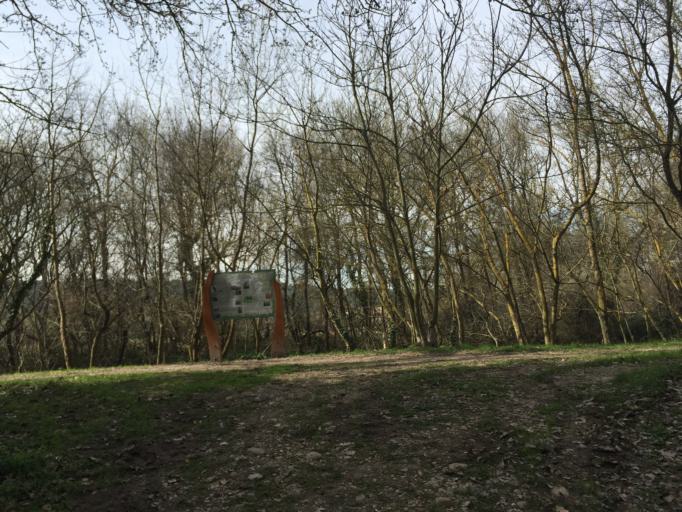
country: FR
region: Provence-Alpes-Cote d'Azur
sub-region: Departement du Vaucluse
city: Bedarrides
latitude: 44.0255
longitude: 4.9123
